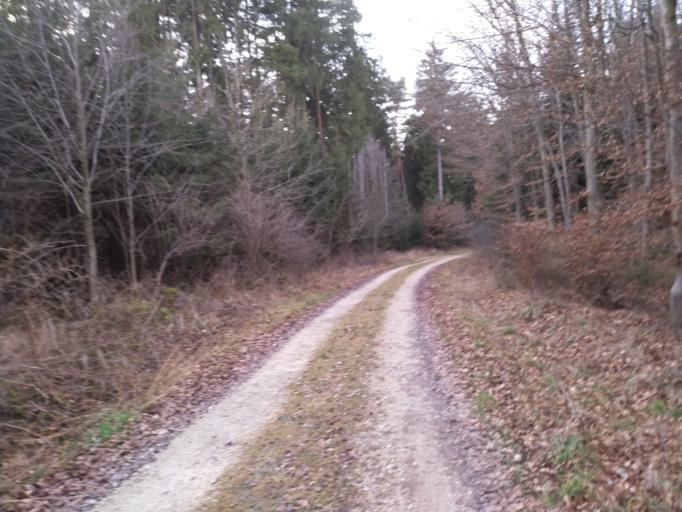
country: DE
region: Bavaria
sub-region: Swabia
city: Rettenbach
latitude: 48.4291
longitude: 10.3172
